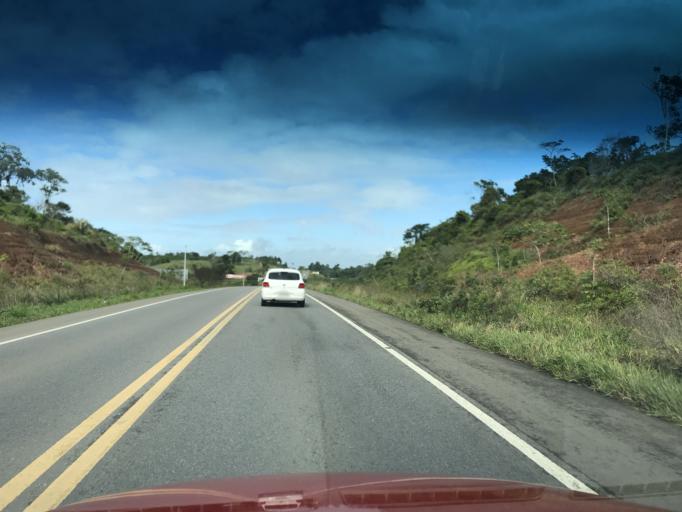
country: BR
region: Bahia
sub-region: Conceicao Do Almeida
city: Muritiba
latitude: -12.9122
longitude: -39.2418
